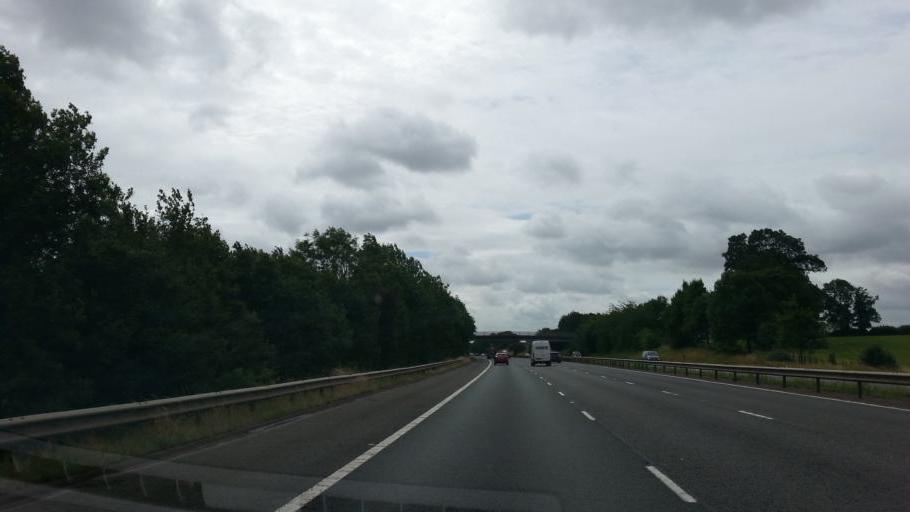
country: GB
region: England
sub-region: Oxfordshire
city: Adderbury
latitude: 52.0267
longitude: -1.2972
